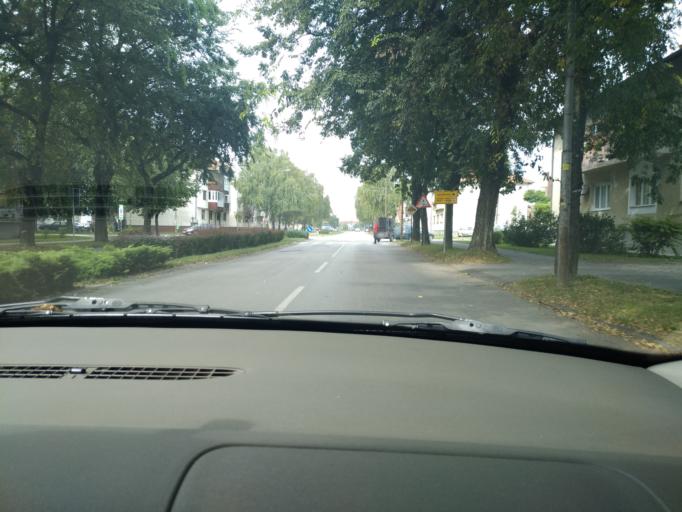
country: BA
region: Federation of Bosnia and Herzegovina
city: Odzak
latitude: 44.9574
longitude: 18.3023
